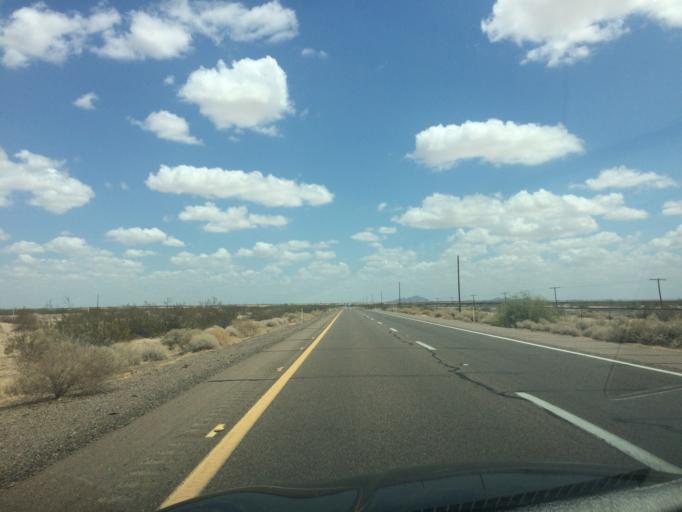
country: US
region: Arizona
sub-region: Yuma County
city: Wellton
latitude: 32.7434
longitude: -113.6802
